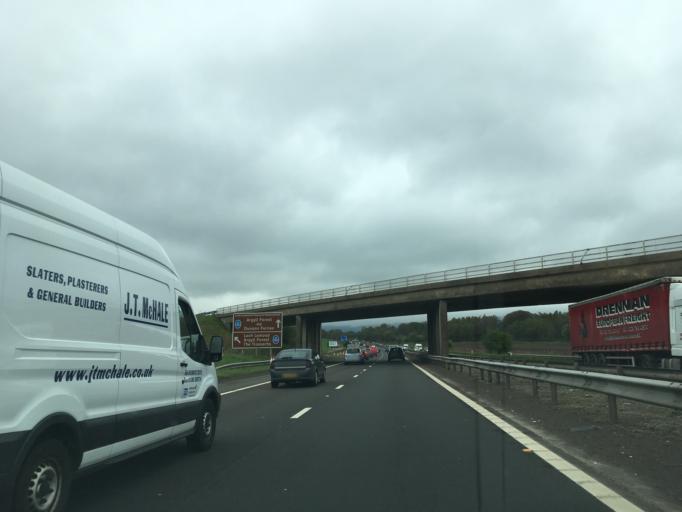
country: GB
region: Scotland
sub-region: Renfrewshire
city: Bishopton
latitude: 55.8915
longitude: -4.4807
